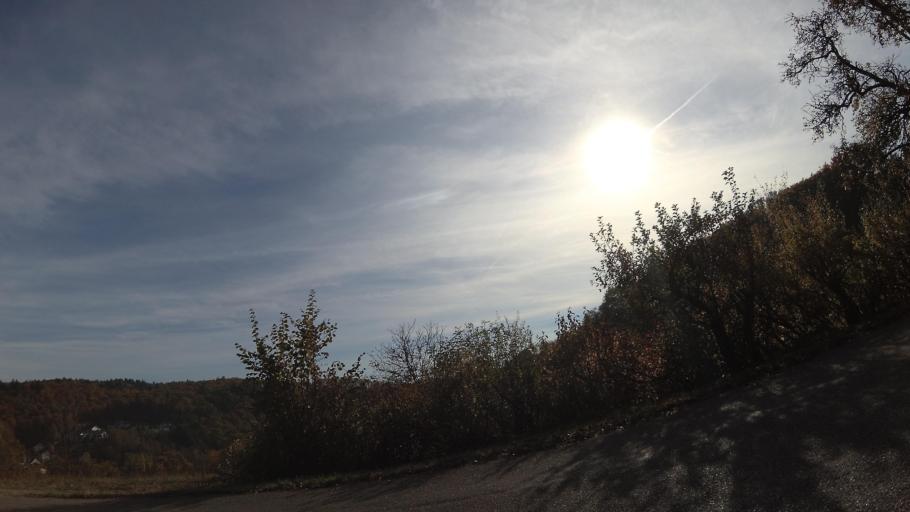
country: DE
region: Baden-Wuerttemberg
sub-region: Karlsruhe Region
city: Billigheim
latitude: 49.3191
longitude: 9.2411
